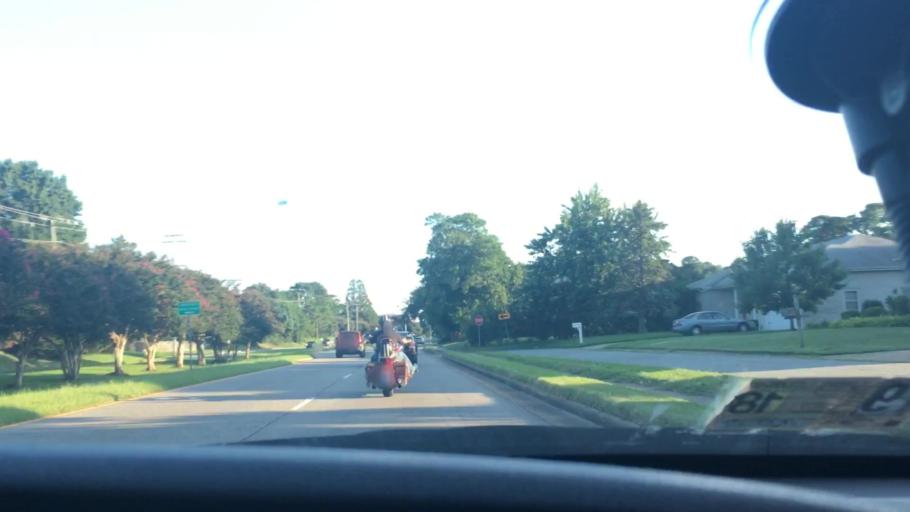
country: US
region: Virginia
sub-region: City of Chesapeake
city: Chesapeake
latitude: 36.8808
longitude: -76.1332
